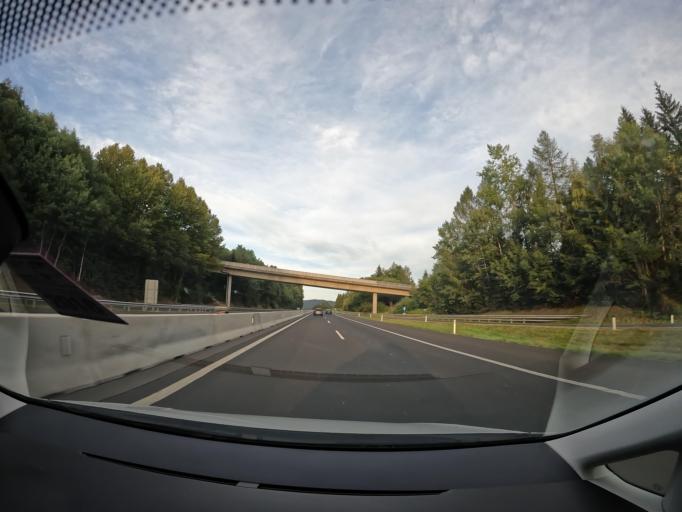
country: AT
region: Carinthia
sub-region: Politischer Bezirk Wolfsberg
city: Preitenegg
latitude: 46.9632
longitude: 14.9115
